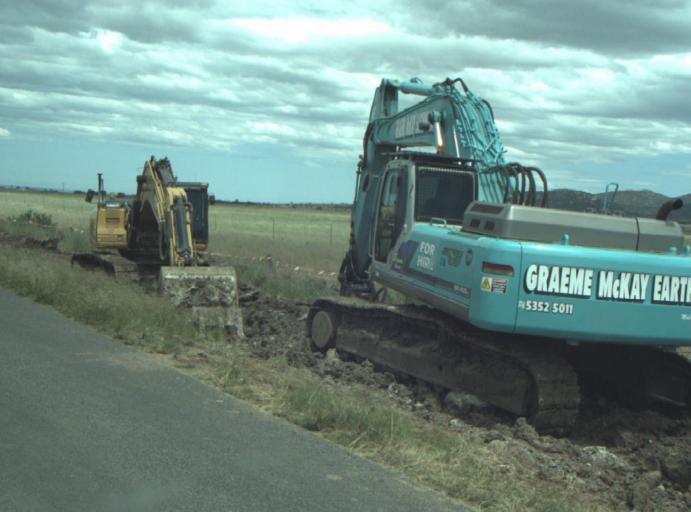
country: AU
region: Victoria
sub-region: Wyndham
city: Little River
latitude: -37.8940
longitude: 144.4632
